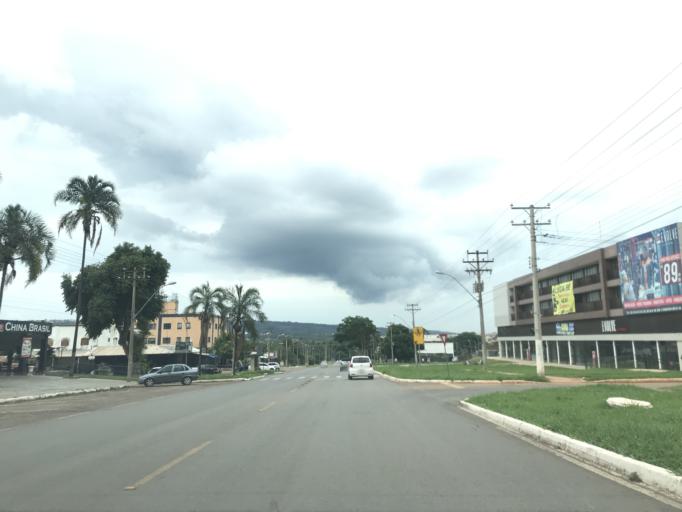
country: BR
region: Federal District
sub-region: Brasilia
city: Brasilia
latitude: -15.6556
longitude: -47.8099
